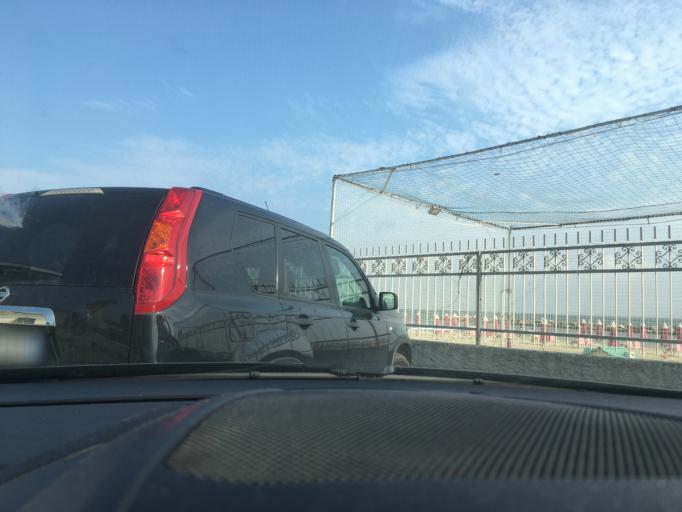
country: IT
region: Emilia-Romagna
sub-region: Provincia di Rimini
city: Santa Giustina
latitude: 44.1063
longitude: 12.5146
